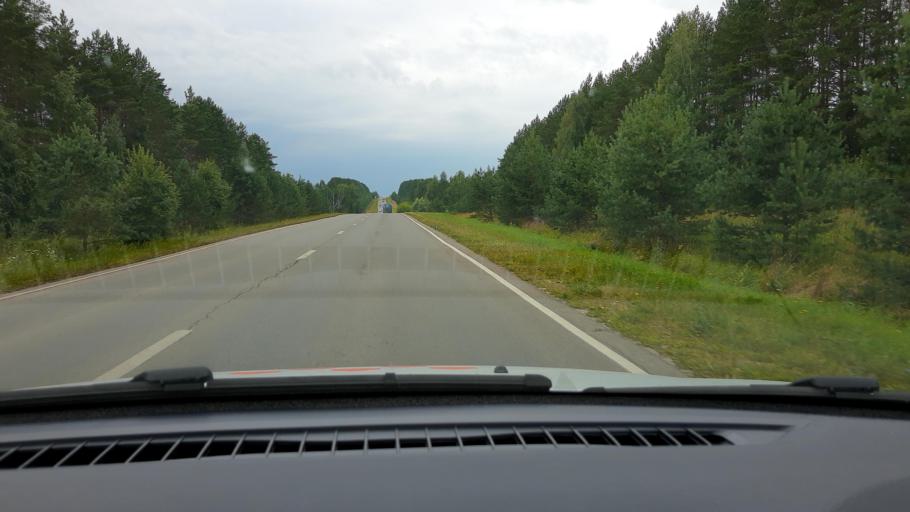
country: RU
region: Nizjnij Novgorod
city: Vyyezdnoye
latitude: 55.1636
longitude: 43.5860
